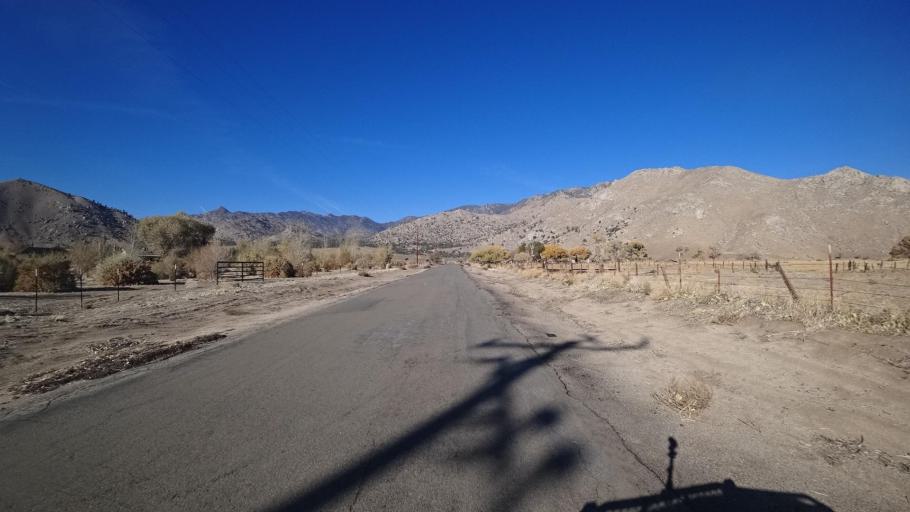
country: US
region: California
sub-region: Kern County
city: Weldon
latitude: 35.6847
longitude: -118.2895
